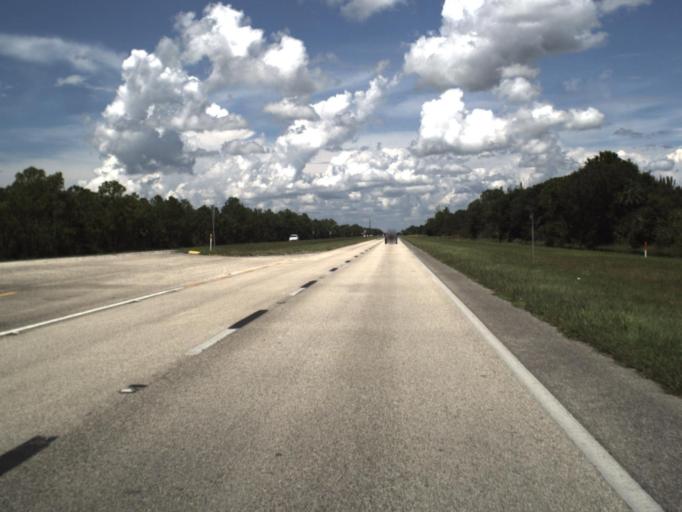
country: US
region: Florida
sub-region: Lee County
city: Burnt Store Marina
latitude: 26.8046
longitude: -81.9533
